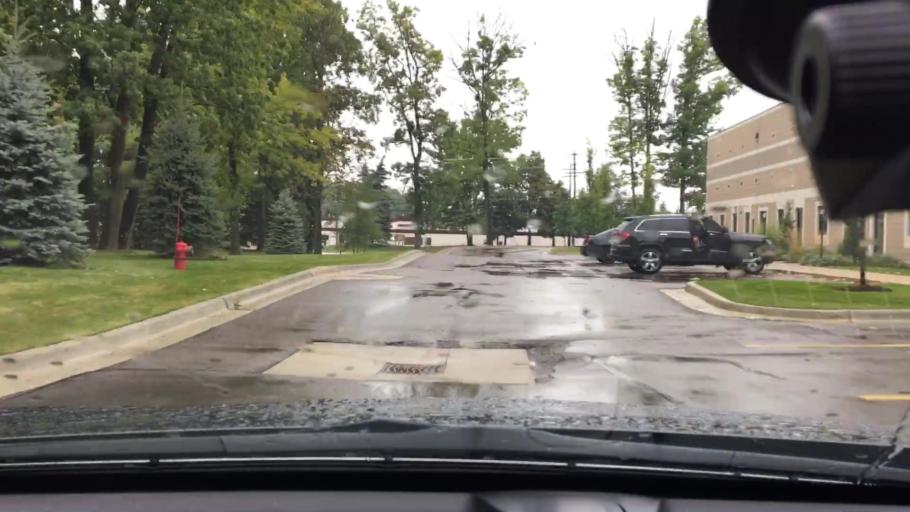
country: US
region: Michigan
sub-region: Oakland County
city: Wixom
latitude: 42.5078
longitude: -83.5195
